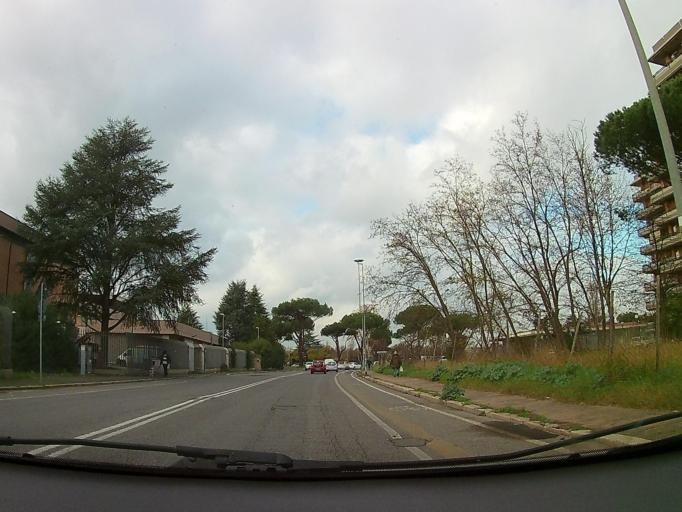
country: IT
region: Latium
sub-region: Citta metropolitana di Roma Capitale
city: Vitinia
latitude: 41.8075
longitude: 12.4445
